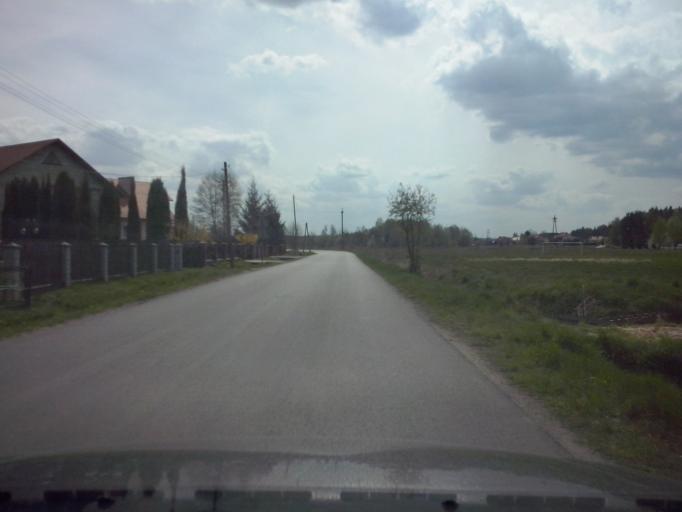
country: PL
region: Subcarpathian Voivodeship
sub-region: Powiat lezajski
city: Letownia
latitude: 50.3492
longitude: 22.2024
